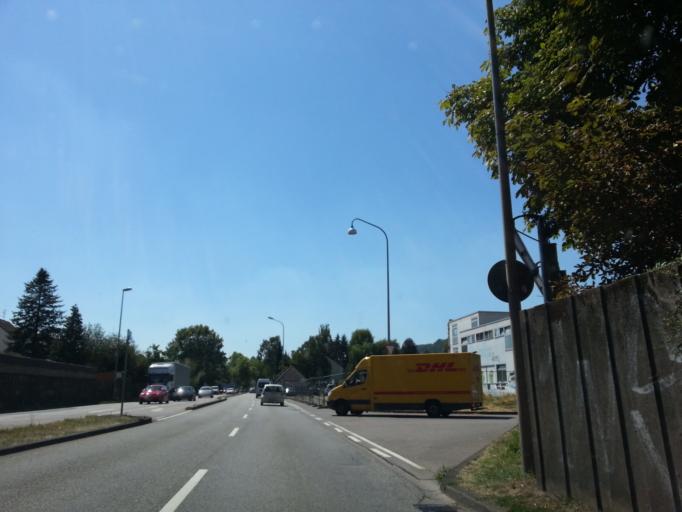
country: DE
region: Rheinland-Pfalz
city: Trier
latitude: 49.7665
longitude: 6.6379
